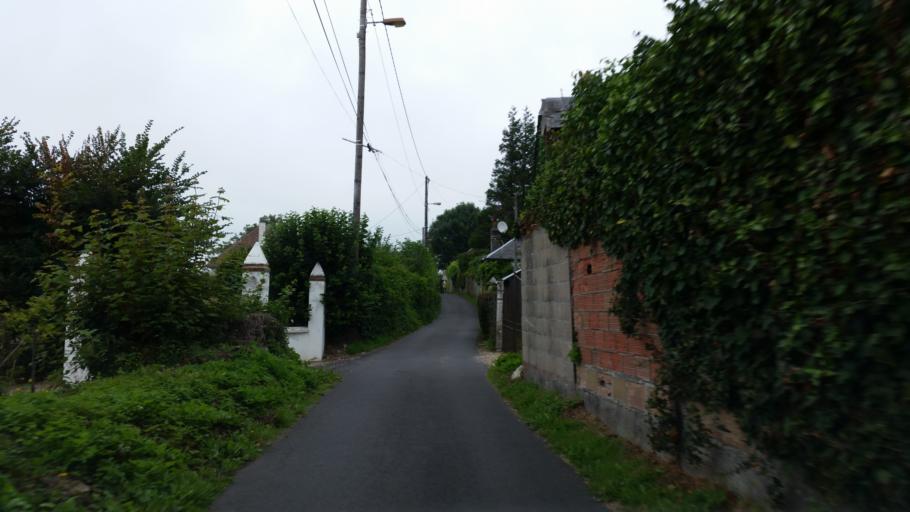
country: FR
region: Lower Normandy
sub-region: Departement du Calvados
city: Honfleur
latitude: 49.4138
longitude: 0.2352
